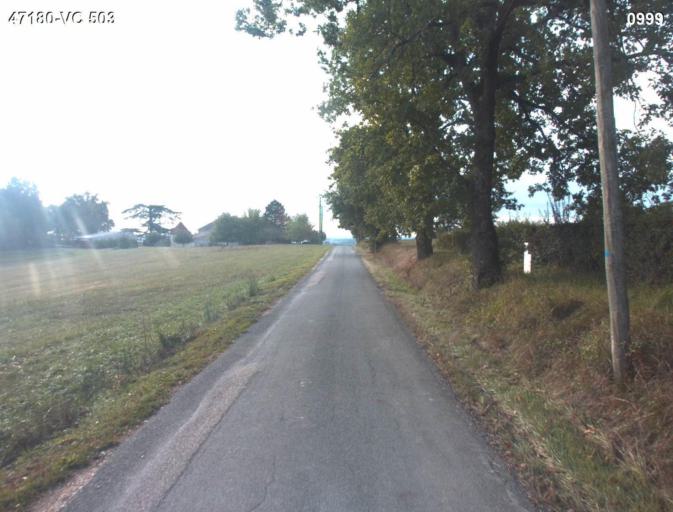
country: FR
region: Aquitaine
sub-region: Departement du Lot-et-Garonne
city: Sainte-Colombe-en-Bruilhois
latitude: 44.1747
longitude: 0.4330
